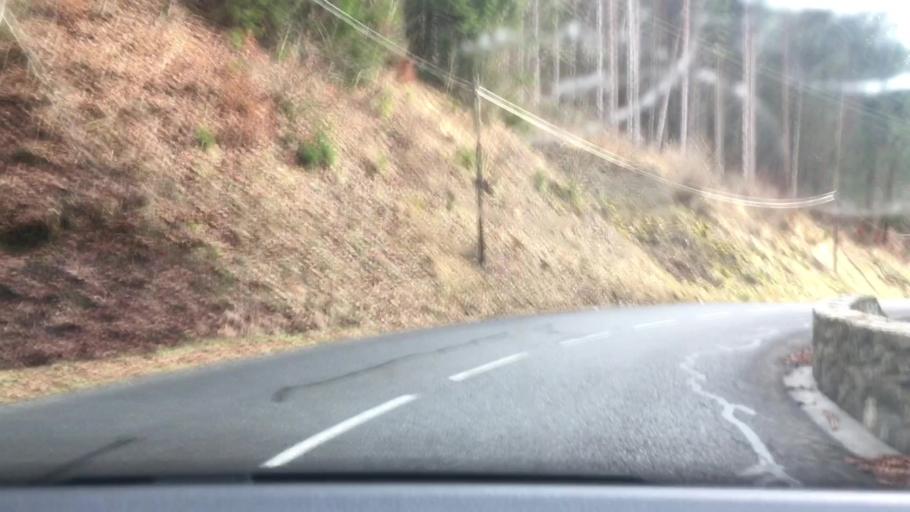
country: FR
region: Rhone-Alpes
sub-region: Departement de la Haute-Savoie
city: Abondance
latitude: 46.2772
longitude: 6.6325
